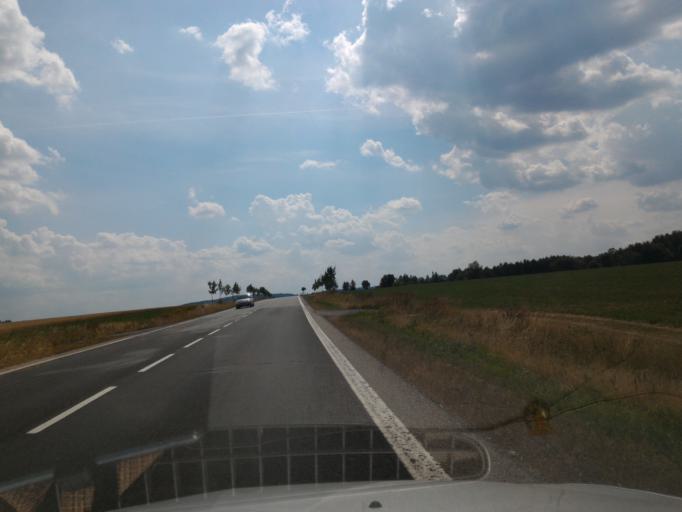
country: CZ
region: Vysocina
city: Bohdalov
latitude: 49.4888
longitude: 15.8856
